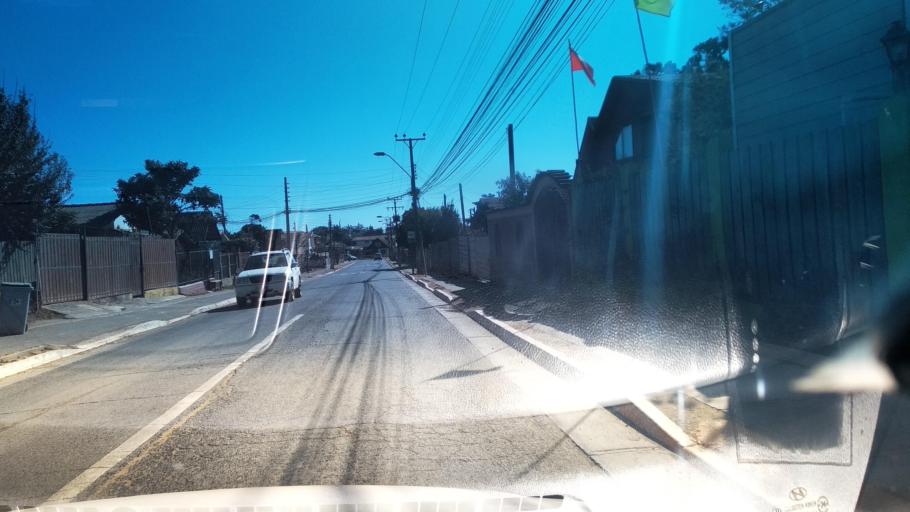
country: CL
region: O'Higgins
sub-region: Provincia de Colchagua
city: Santa Cruz
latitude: -34.3935
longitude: -72.0124
